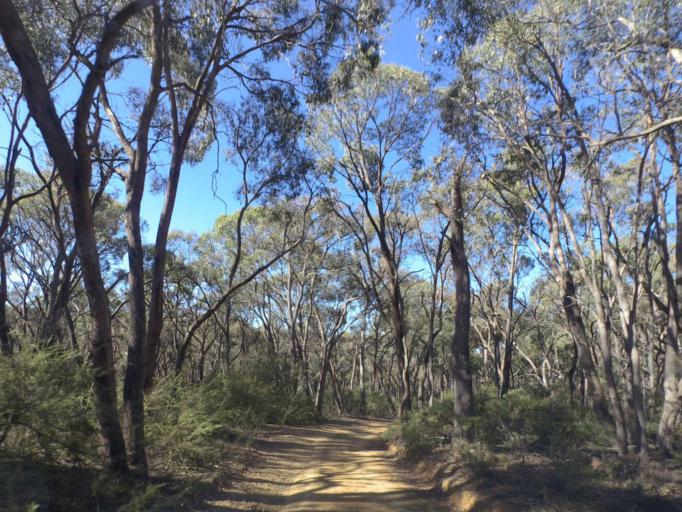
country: AU
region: Victoria
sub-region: Murrindindi
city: Kinglake West
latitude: -37.4636
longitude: 145.3708
